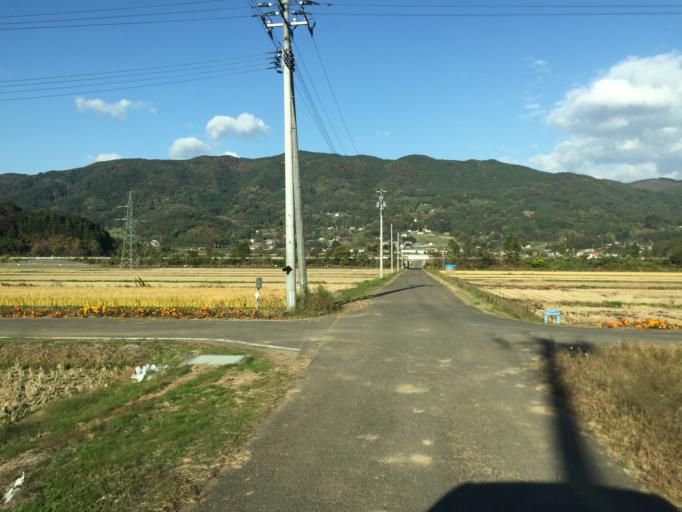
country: JP
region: Fukushima
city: Yanagawamachi-saiwaicho
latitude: 37.9229
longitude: 140.6121
